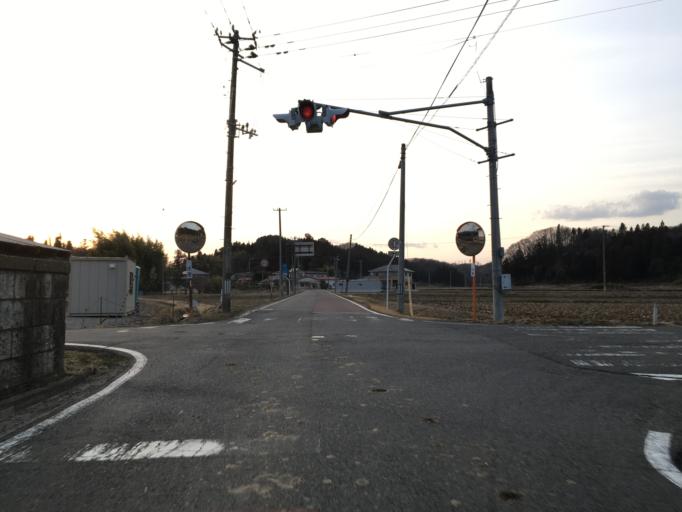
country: JP
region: Fukushima
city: Ishikawa
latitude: 37.0714
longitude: 140.3065
